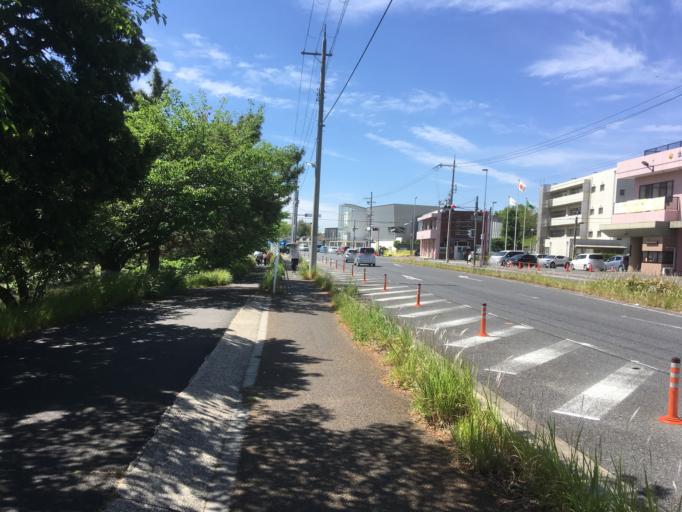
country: JP
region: Nara
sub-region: Ikoma-shi
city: Ikoma
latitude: 34.6679
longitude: 135.7072
